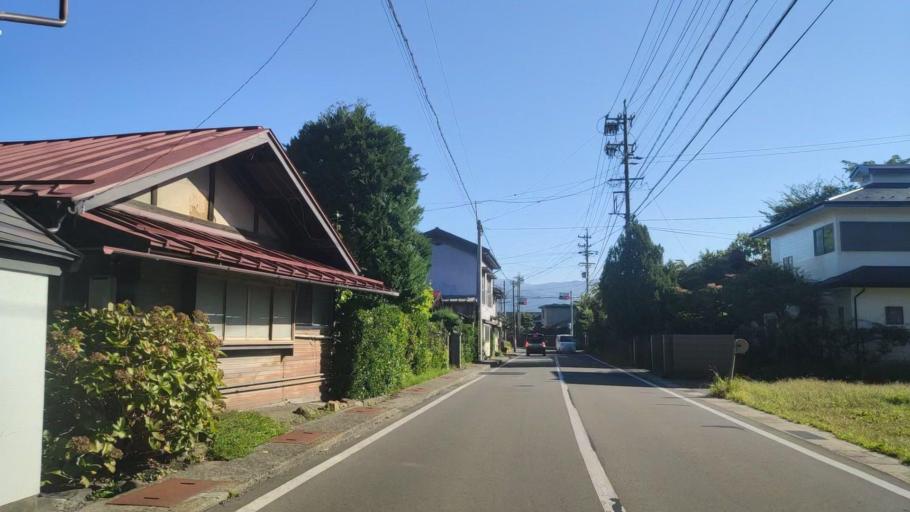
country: JP
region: Nagano
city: Okaya
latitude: 36.0548
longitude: 138.0555
